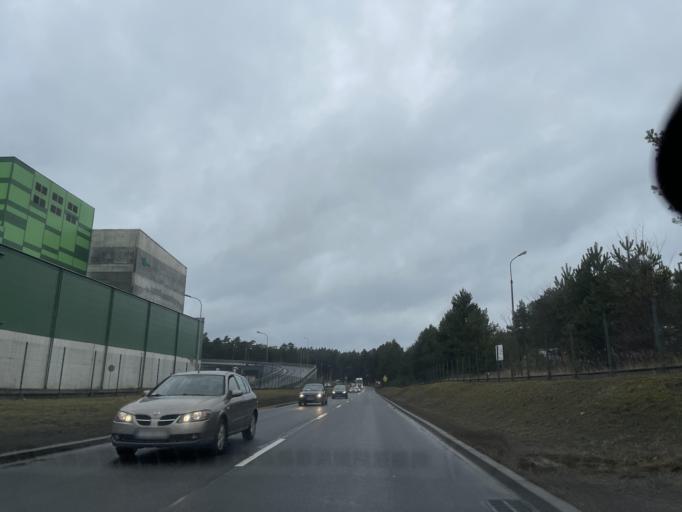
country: PL
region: Kujawsko-Pomorskie
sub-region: Bydgoszcz
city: Bydgoszcz
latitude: 53.0692
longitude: 18.0847
